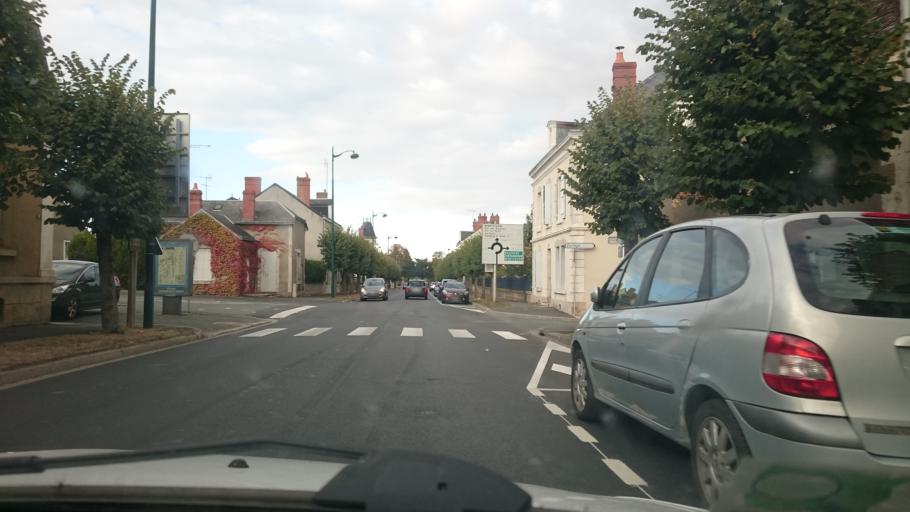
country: FR
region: Centre
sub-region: Departement de l'Indre
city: La Chatre
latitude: 46.5835
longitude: 1.9849
